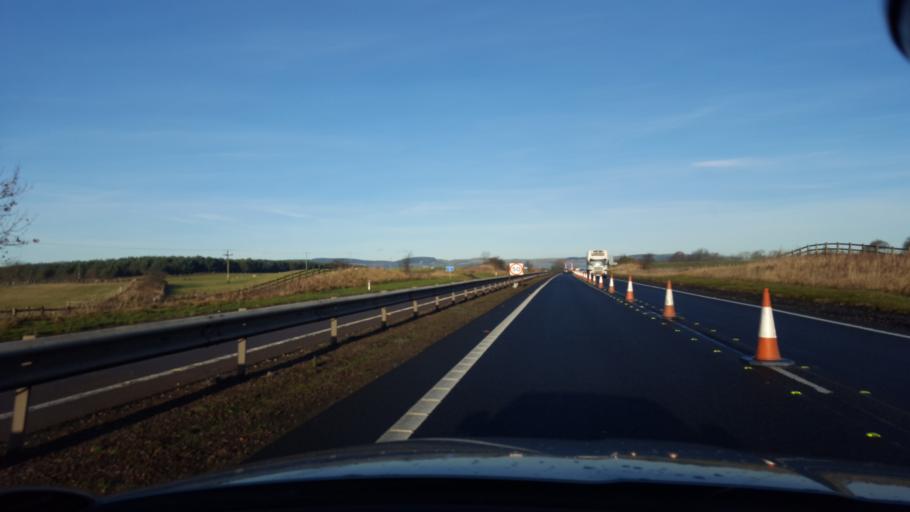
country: GB
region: Scotland
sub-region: Perth and Kinross
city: Kinross
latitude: 56.1824
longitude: -3.4155
